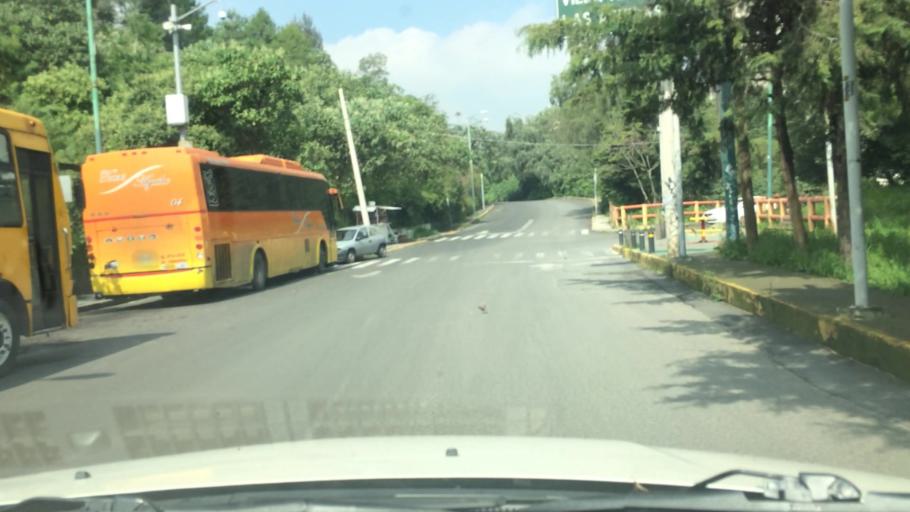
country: MX
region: Mexico City
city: Magdalena Contreras
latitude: 19.3473
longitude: -99.2178
